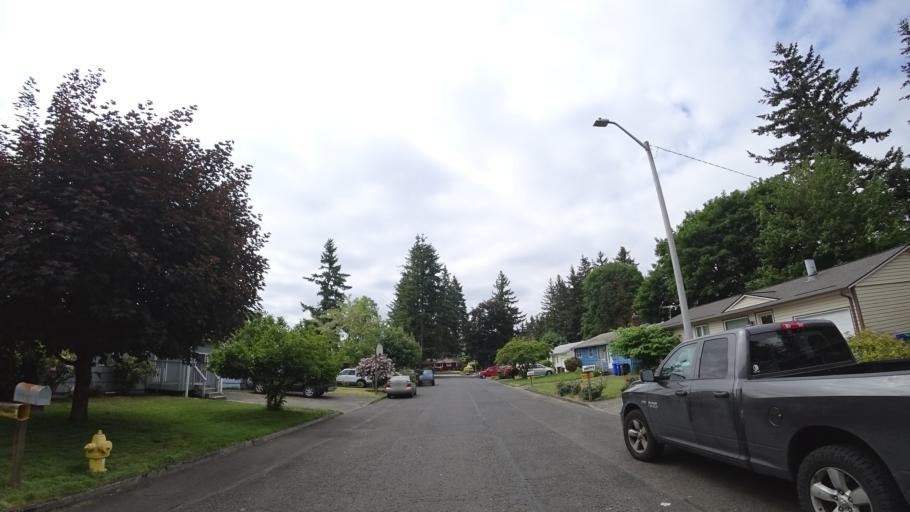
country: US
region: Oregon
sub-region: Multnomah County
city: Gresham
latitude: 45.5022
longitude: -122.4828
